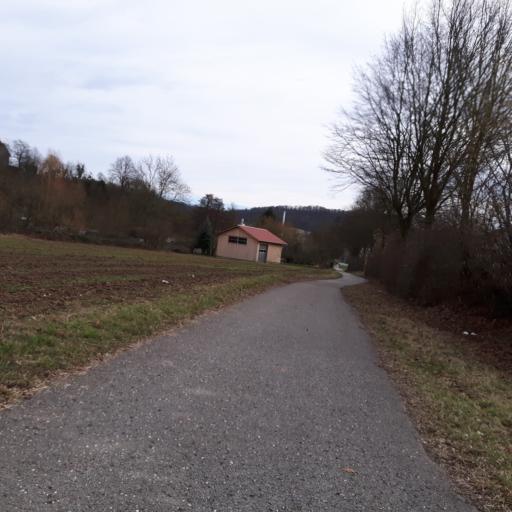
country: DE
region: Baden-Wuerttemberg
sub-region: Regierungsbezirk Stuttgart
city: Oberstenfeld
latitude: 49.0301
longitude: 9.3191
